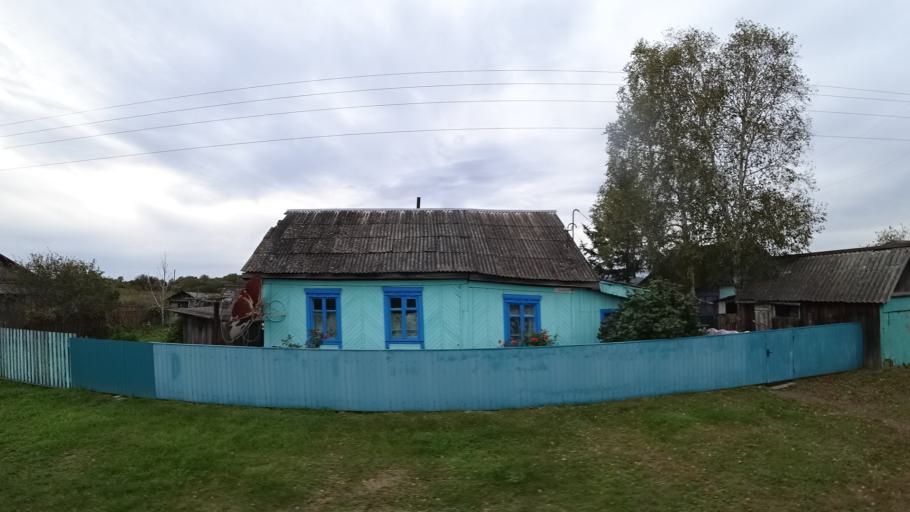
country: RU
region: Amur
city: Arkhara
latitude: 49.4329
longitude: 130.2610
